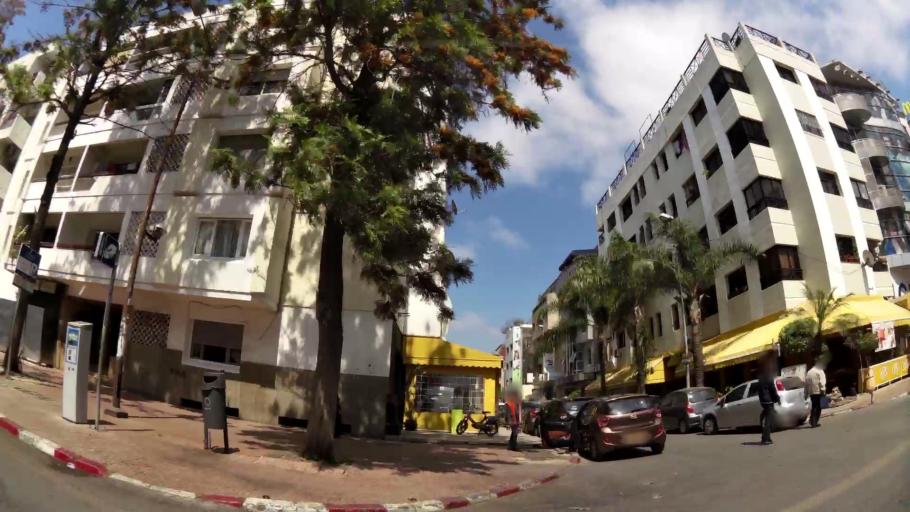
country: MA
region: Rabat-Sale-Zemmour-Zaer
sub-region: Rabat
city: Rabat
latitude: 33.9958
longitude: -6.8477
